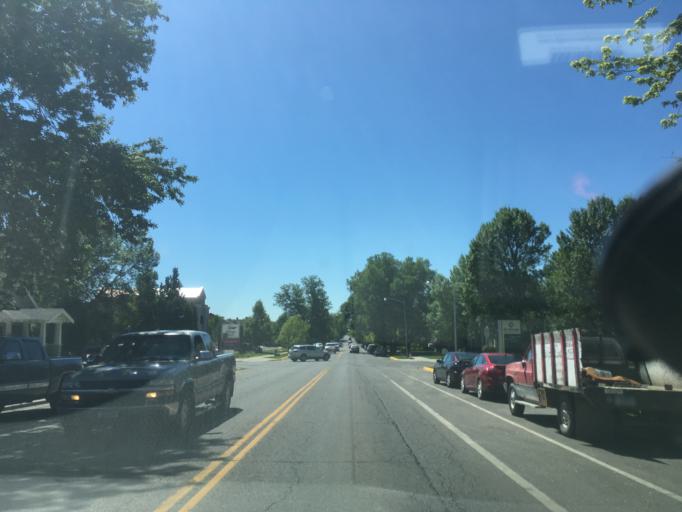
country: US
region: Montana
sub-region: Yellowstone County
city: Billings
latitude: 45.7914
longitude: -108.5186
